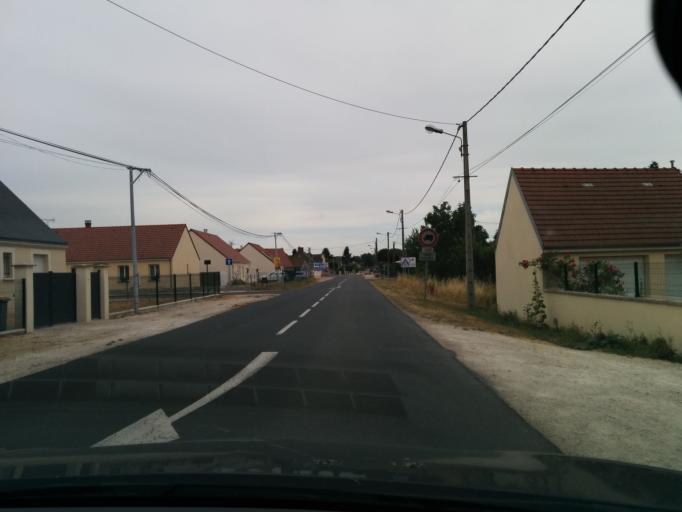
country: FR
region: Centre
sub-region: Departement du Loiret
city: Chateauneuf-sur-Loire
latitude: 47.8694
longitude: 2.2052
